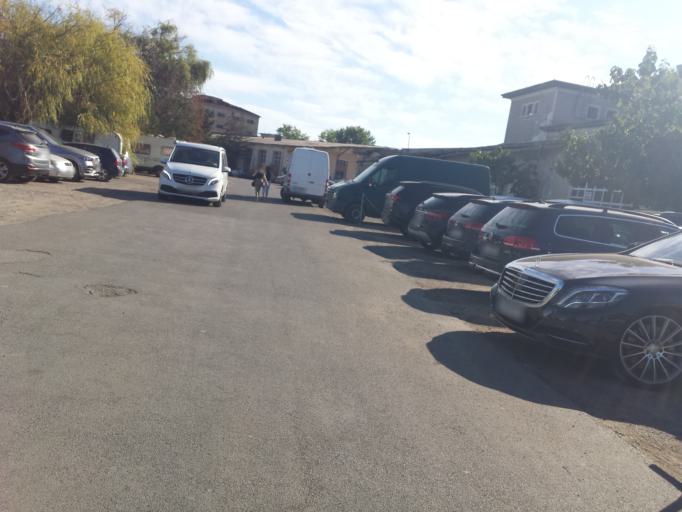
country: RO
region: Tulcea
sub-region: Municipiul Tulcea
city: Tulcea
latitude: 45.1823
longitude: 28.8062
